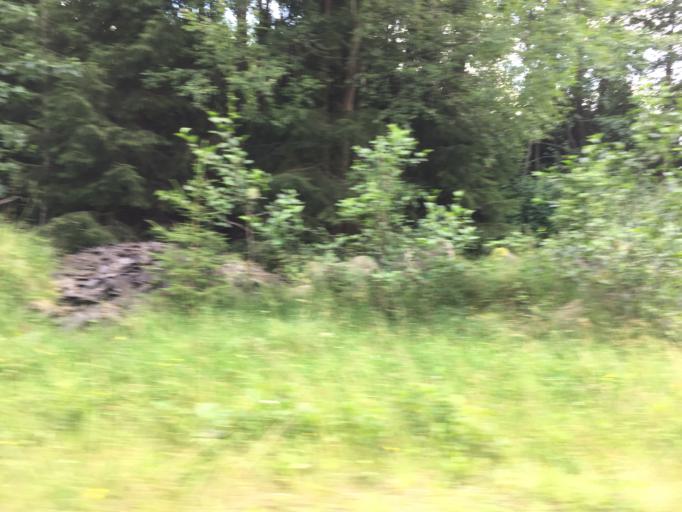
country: SE
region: Soedermanland
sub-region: Vingakers Kommun
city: Vingaker
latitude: 58.9829
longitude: 15.6975
